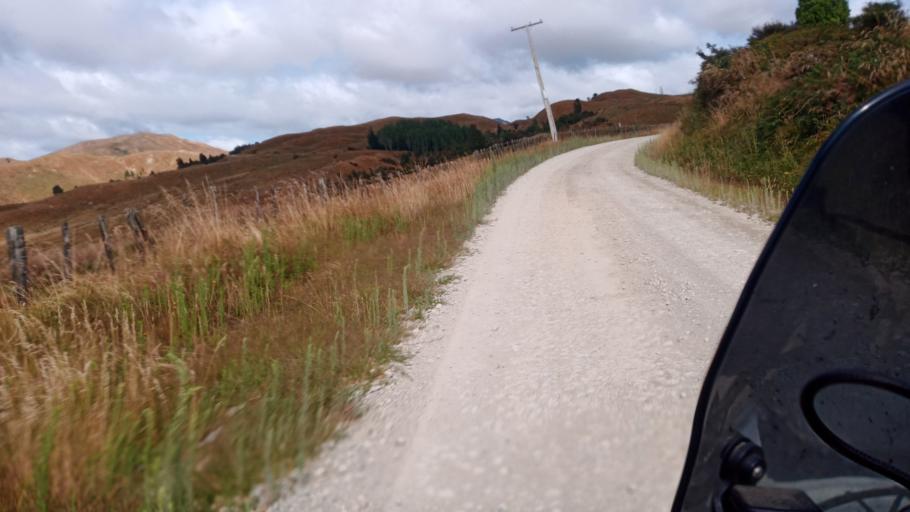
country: NZ
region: Hawke's Bay
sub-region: Wairoa District
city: Wairoa
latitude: -38.6040
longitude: 177.4725
